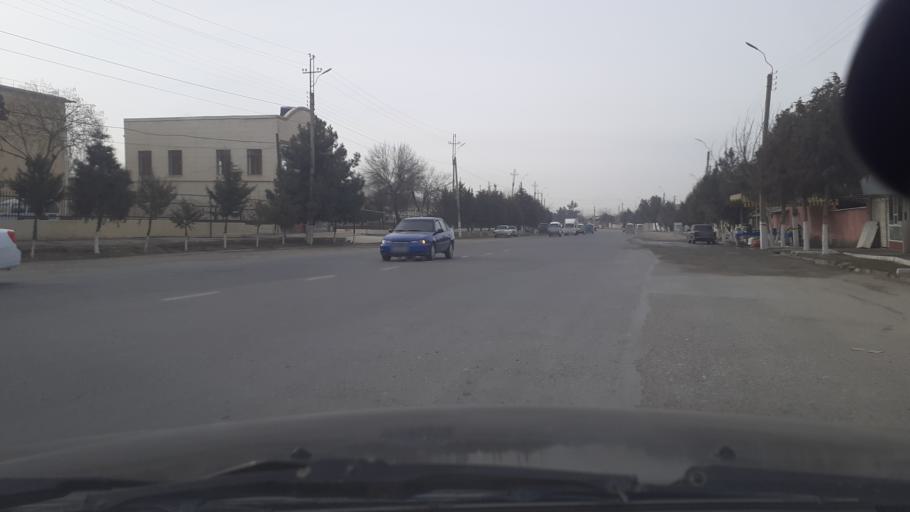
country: UZ
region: Namangan
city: Namangan
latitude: 41.0441
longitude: 71.6776
